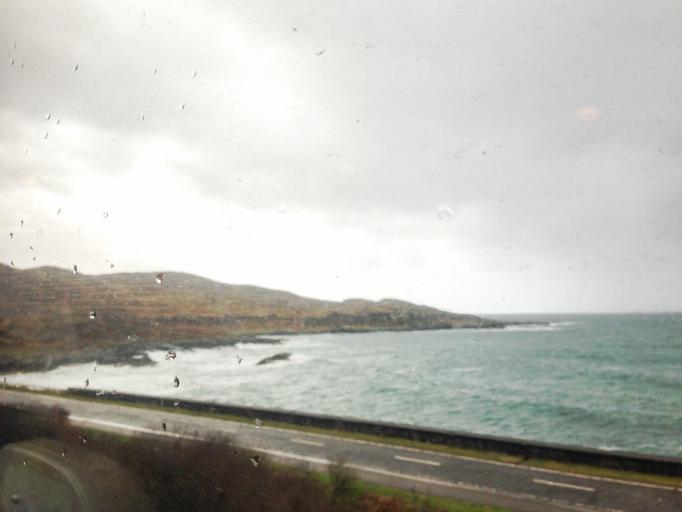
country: GB
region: Scotland
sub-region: Argyll and Bute
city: Isle Of Mull
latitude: 56.9963
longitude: -5.8316
